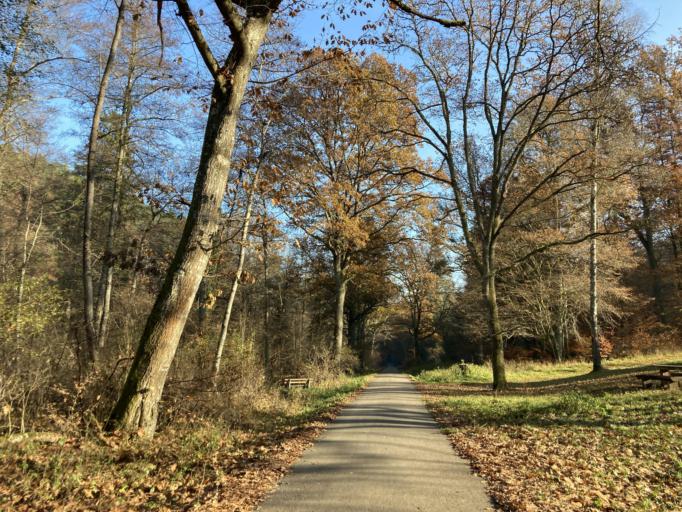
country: DE
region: Baden-Wuerttemberg
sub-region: Tuebingen Region
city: Tuebingen
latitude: 48.5574
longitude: 9.0155
